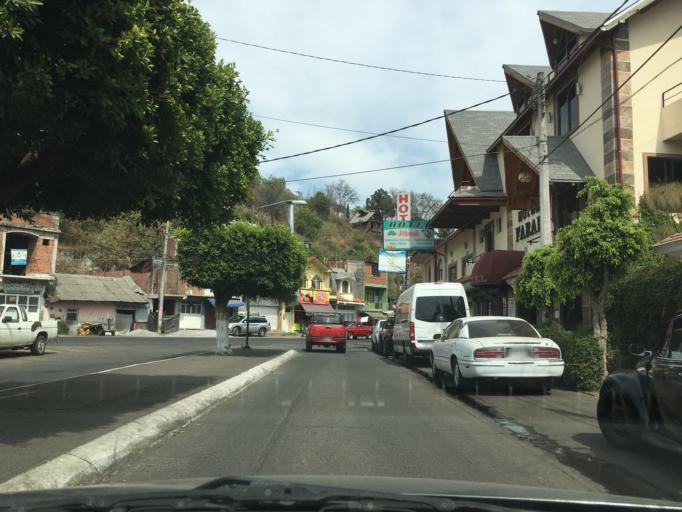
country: MX
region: Michoacan
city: Nuevo San Juan Parangaricutiro
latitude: 19.4157
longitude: -102.1255
